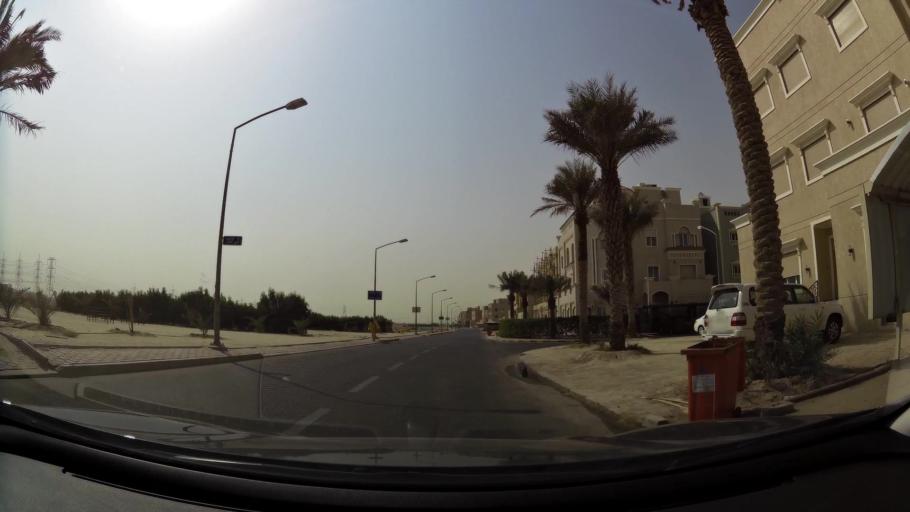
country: KW
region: Muhafazat al Jahra'
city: Al Jahra'
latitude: 29.3303
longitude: 47.7807
